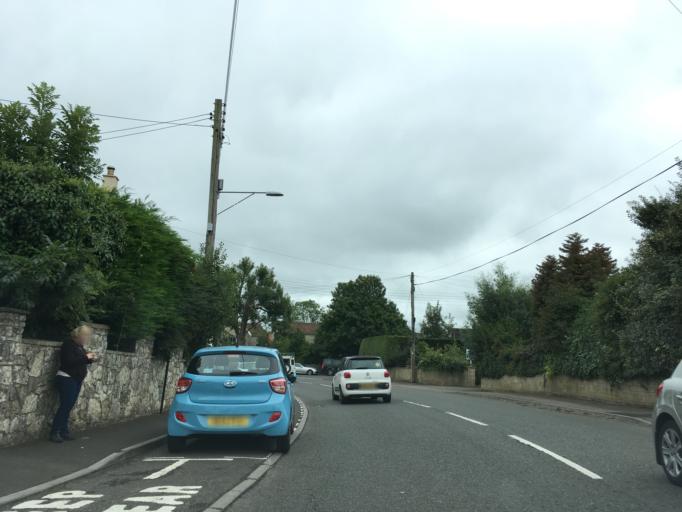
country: GB
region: England
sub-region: Bath and North East Somerset
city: Paulton
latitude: 51.3247
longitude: -2.5113
